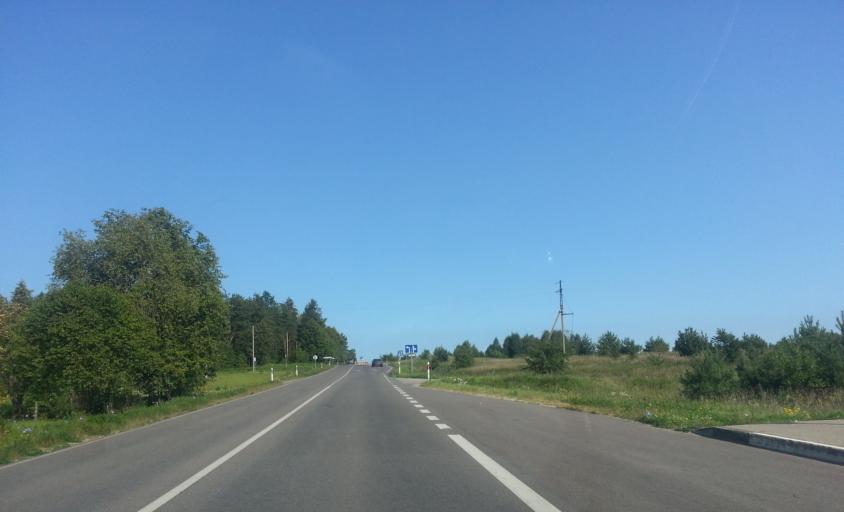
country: LT
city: Grigiskes
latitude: 54.7523
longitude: 25.0815
